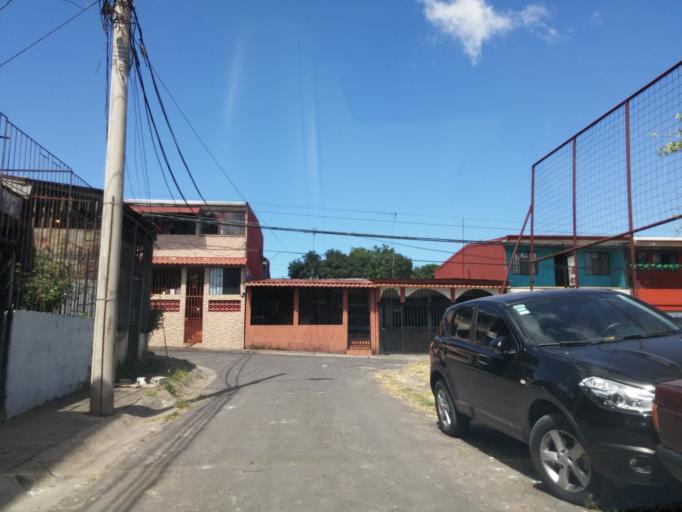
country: CR
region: San Jose
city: San Felipe
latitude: 9.9165
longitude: -84.1160
